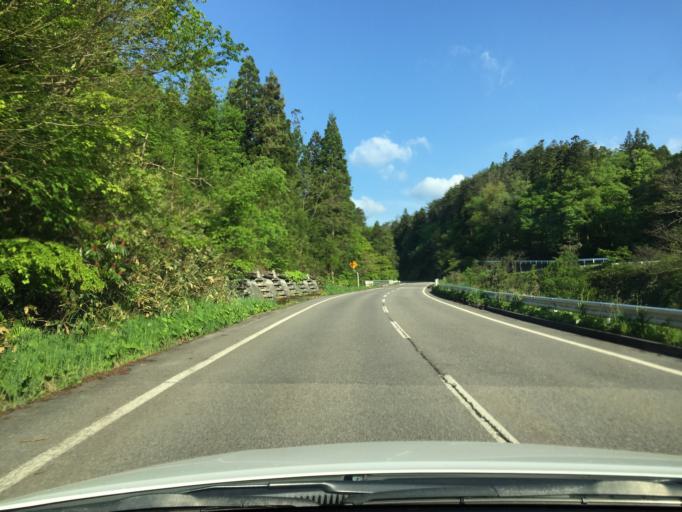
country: JP
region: Fukushima
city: Kitakata
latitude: 37.6670
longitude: 139.8441
